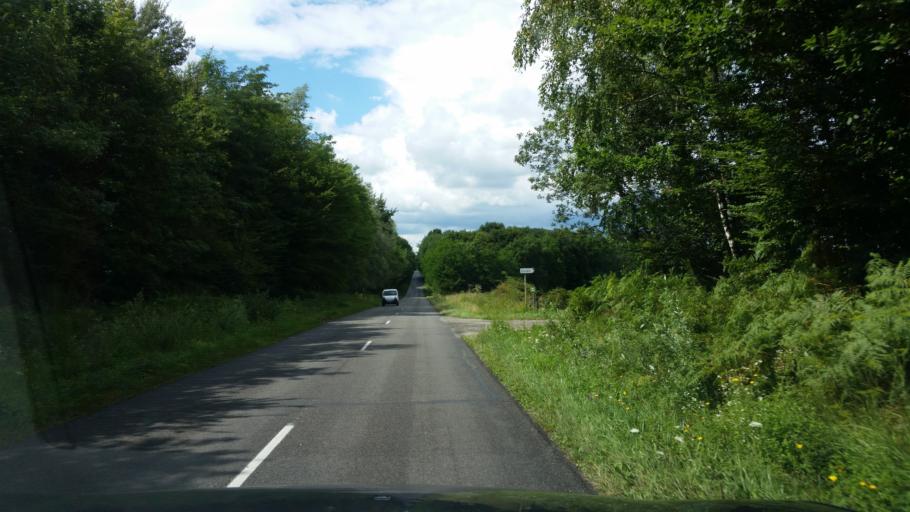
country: FR
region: Franche-Comte
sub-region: Departement du Jura
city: Bletterans
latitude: 46.6808
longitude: 5.3830
